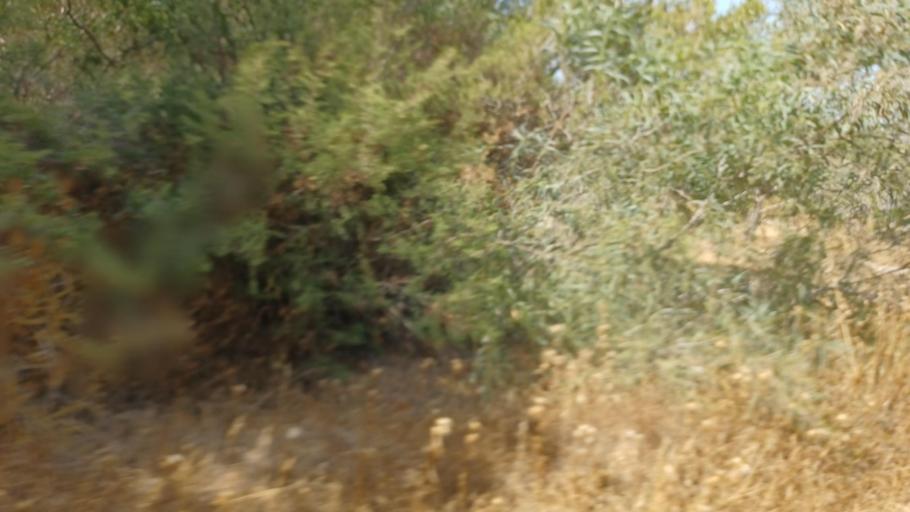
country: CY
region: Ammochostos
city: Paralimni
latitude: 35.0044
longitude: 33.9588
